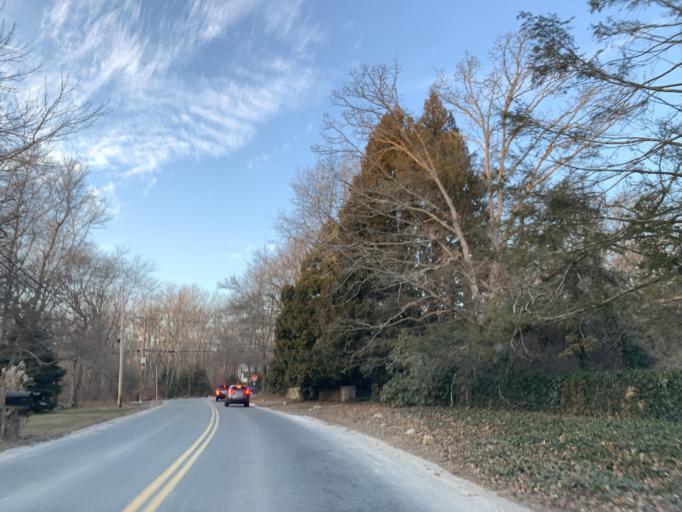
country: US
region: Rhode Island
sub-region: Washington County
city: Kingston
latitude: 41.4826
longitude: -71.4999
